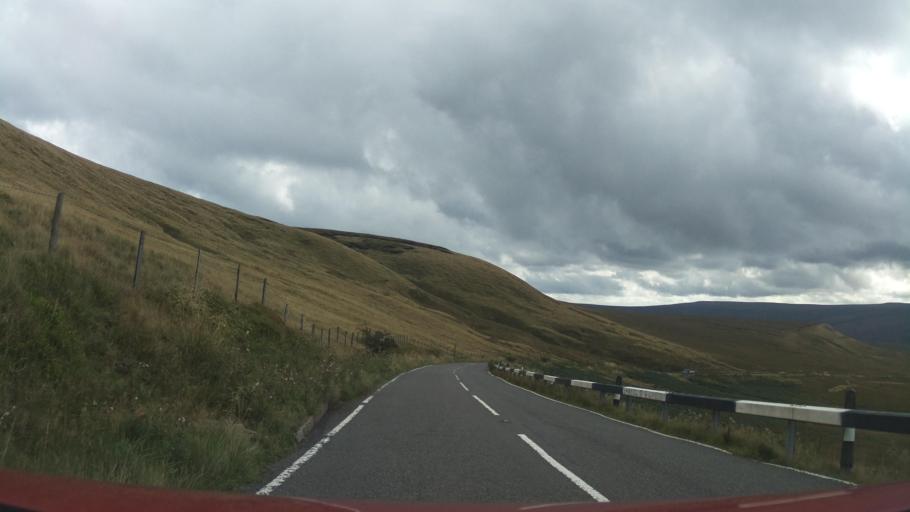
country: GB
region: England
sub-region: Kirklees
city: Meltham
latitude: 53.5249
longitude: -1.8539
